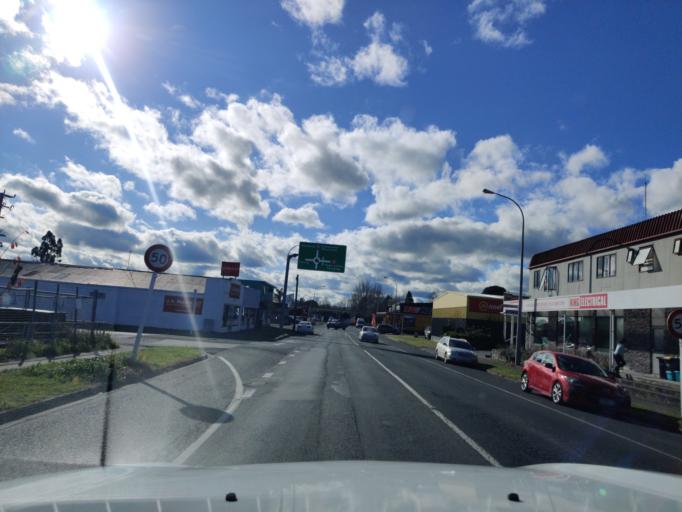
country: NZ
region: Waikato
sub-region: Matamata-Piako District
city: Matamata
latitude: -37.8102
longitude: 175.7706
